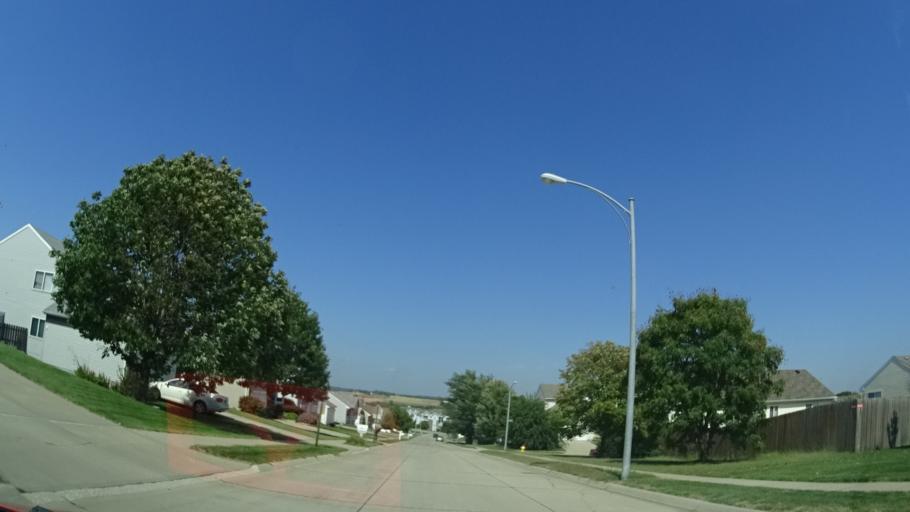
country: US
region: Nebraska
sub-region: Sarpy County
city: Offutt Air Force Base
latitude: 41.1334
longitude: -95.9551
